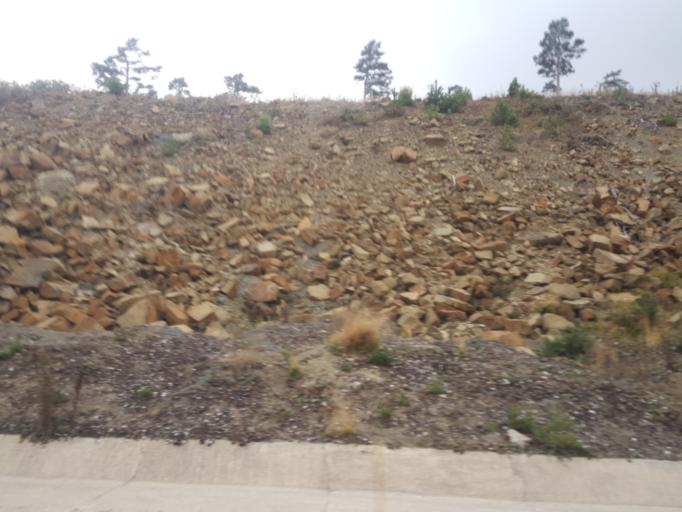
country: TR
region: Sinop
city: Duragan
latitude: 41.5161
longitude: 35.1091
